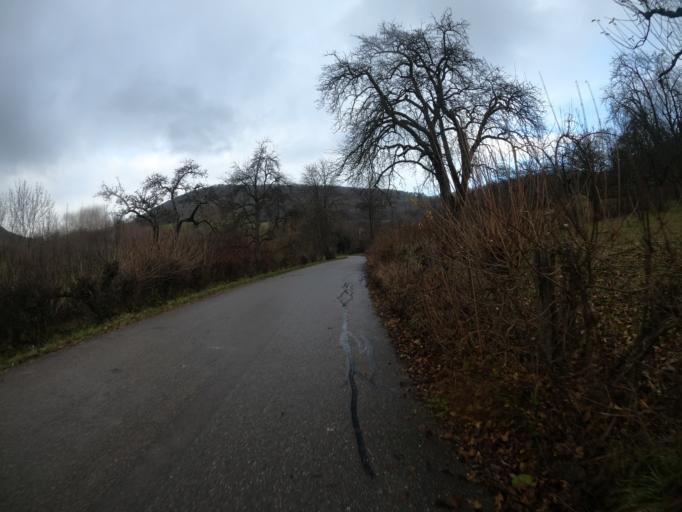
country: DE
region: Baden-Wuerttemberg
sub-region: Regierungsbezirk Stuttgart
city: Donzdorf
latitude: 48.7171
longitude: 9.8593
